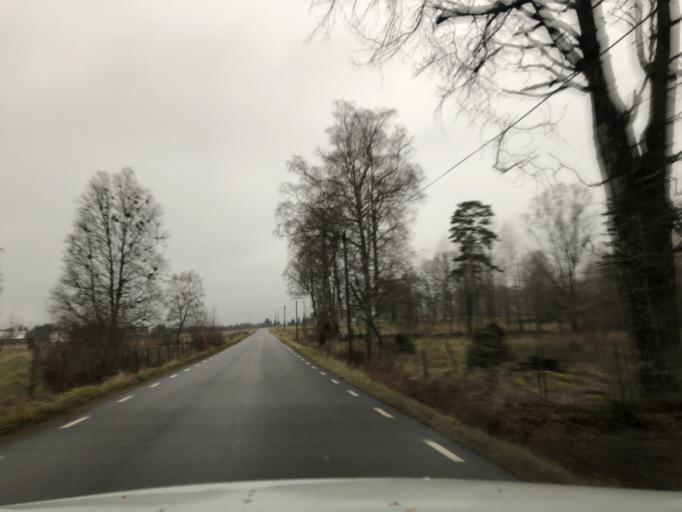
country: SE
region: Vaestra Goetaland
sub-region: Ulricehamns Kommun
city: Ulricehamn
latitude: 57.8389
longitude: 13.3802
